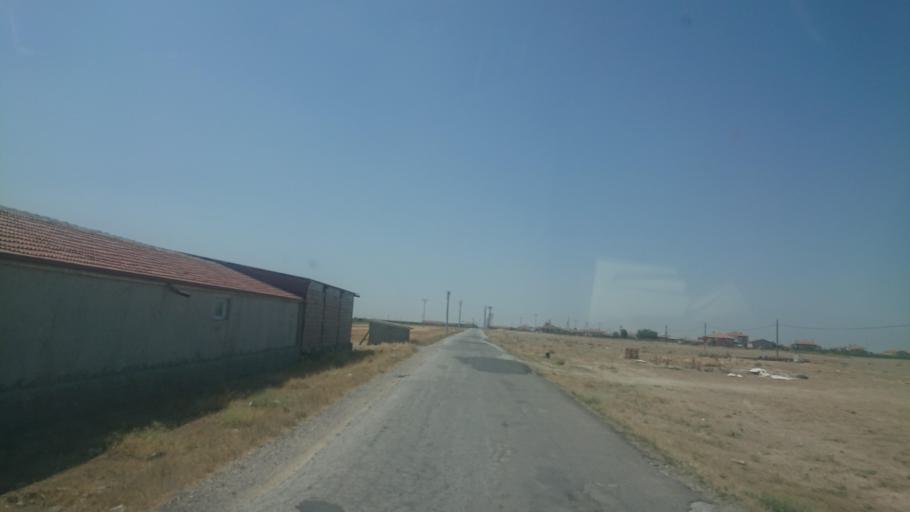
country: TR
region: Aksaray
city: Yesilova
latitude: 38.2919
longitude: 33.7211
